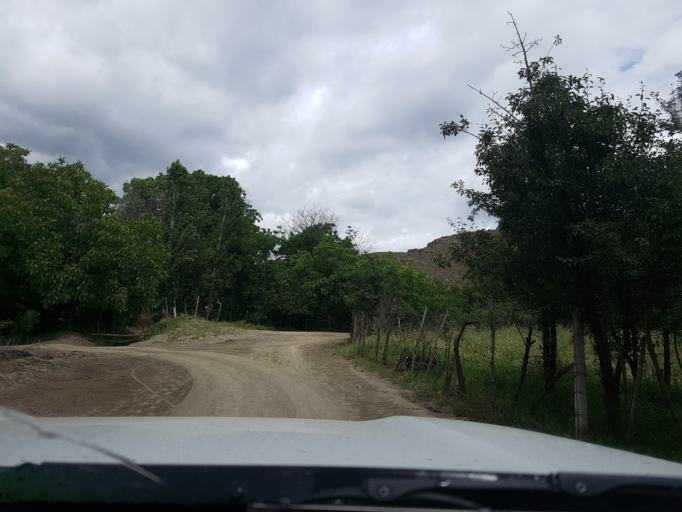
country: TM
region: Ahal
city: Baharly
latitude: 38.1944
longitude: 57.0064
